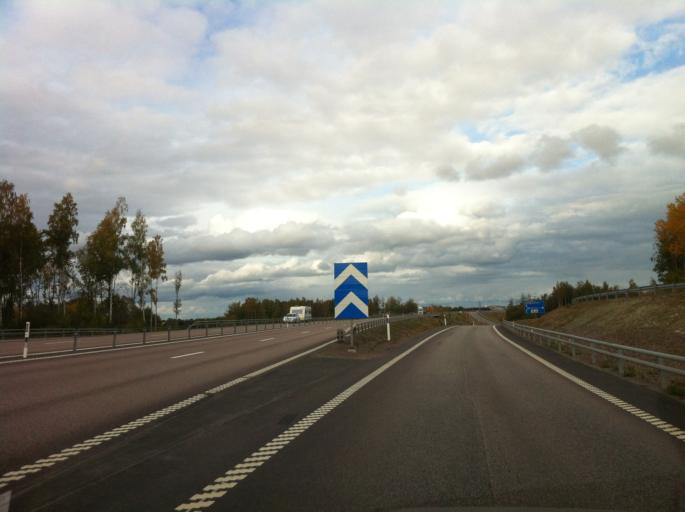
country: SE
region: OEstergoetland
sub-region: Motala Kommun
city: Motala
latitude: 58.5195
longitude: 15.0138
